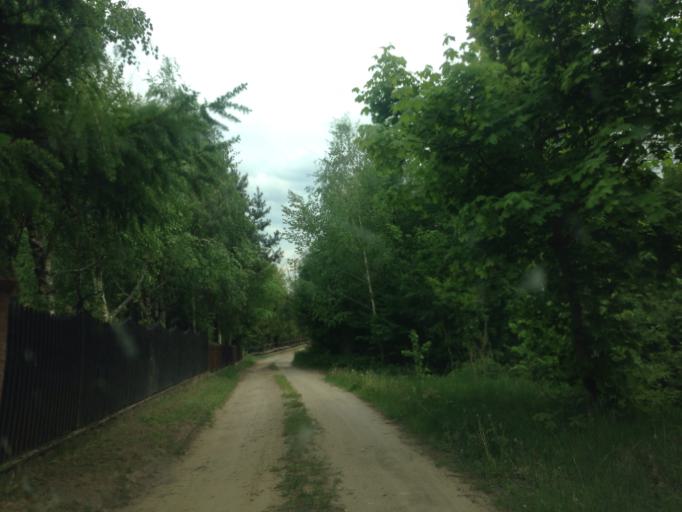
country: PL
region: Kujawsko-Pomorskie
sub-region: Powiat brodnicki
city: Brodnica
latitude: 53.3230
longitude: 19.3661
